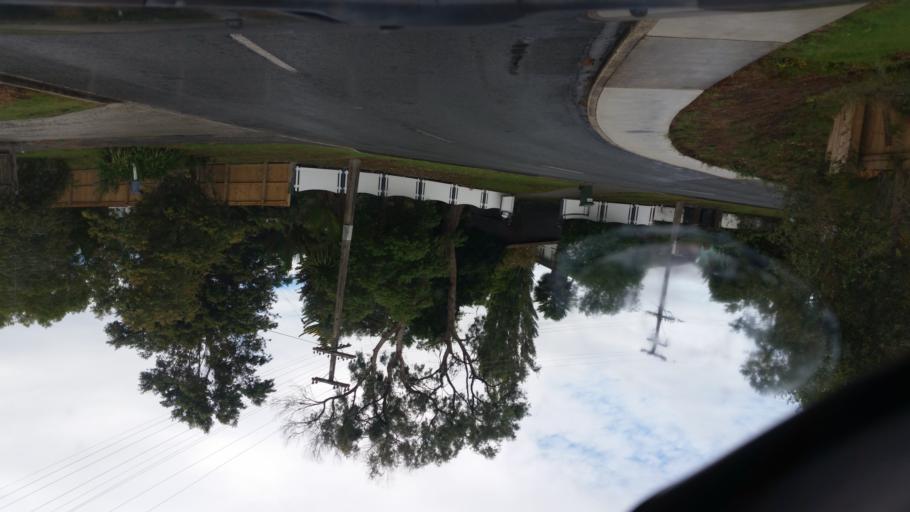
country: NZ
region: Northland
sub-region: Whangarei
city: Ruakaka
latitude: -36.1081
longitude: 174.3619
